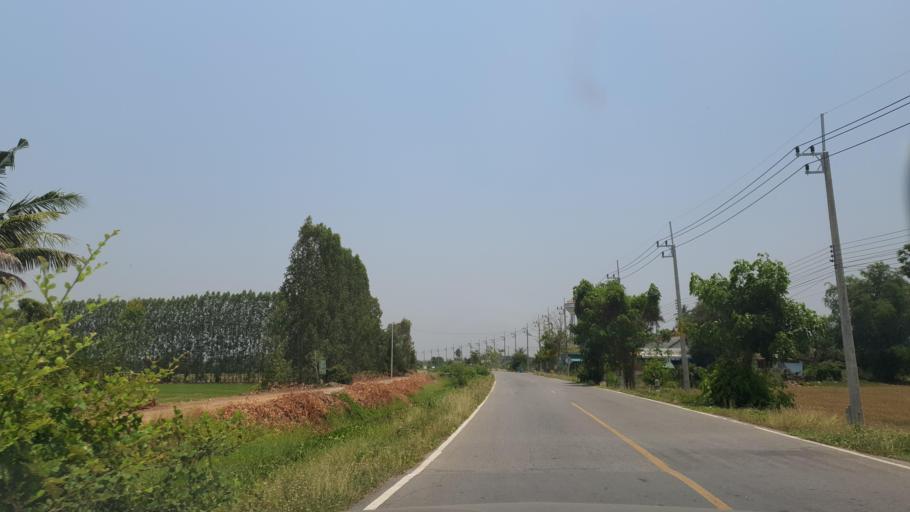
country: TH
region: Suphan Buri
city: Si Prachan
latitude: 14.5824
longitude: 100.1081
